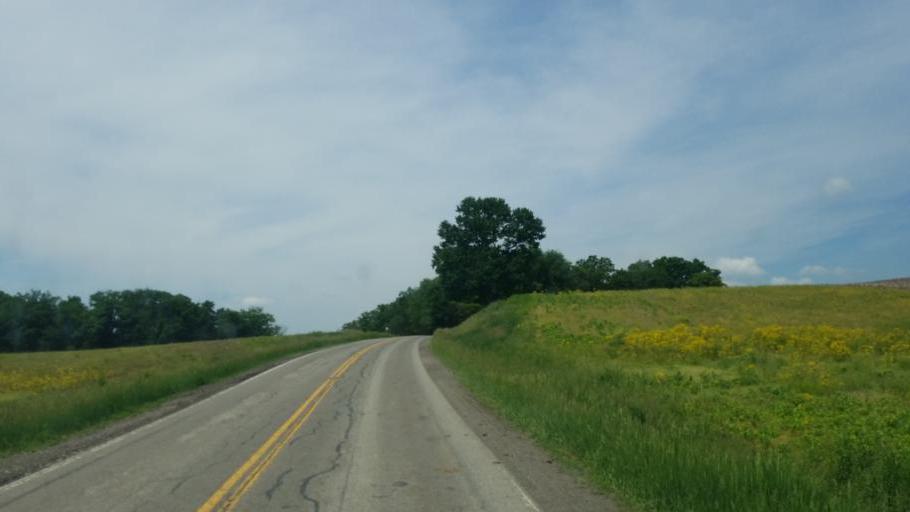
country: US
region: Ohio
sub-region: Tuscarawas County
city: Sugarcreek
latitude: 40.4412
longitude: -81.7733
